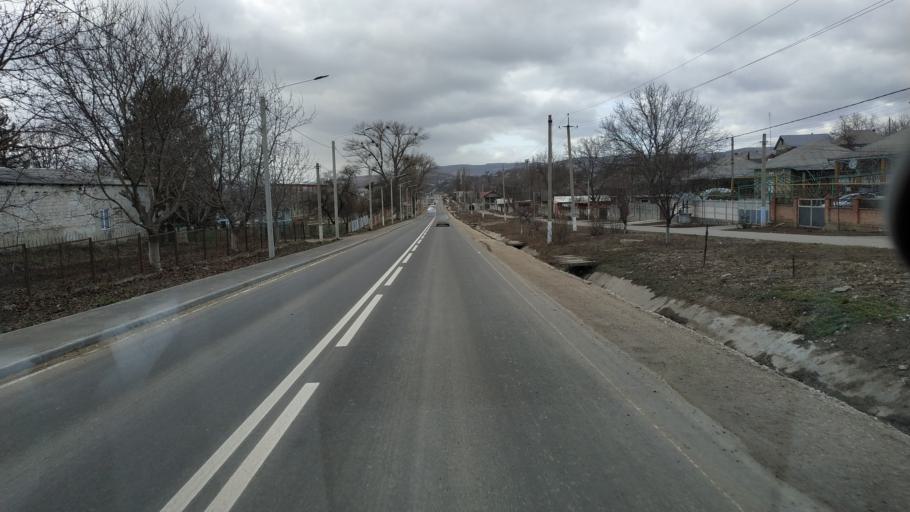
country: MD
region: Calarasi
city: Calarasi
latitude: 47.2774
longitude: 28.2139
